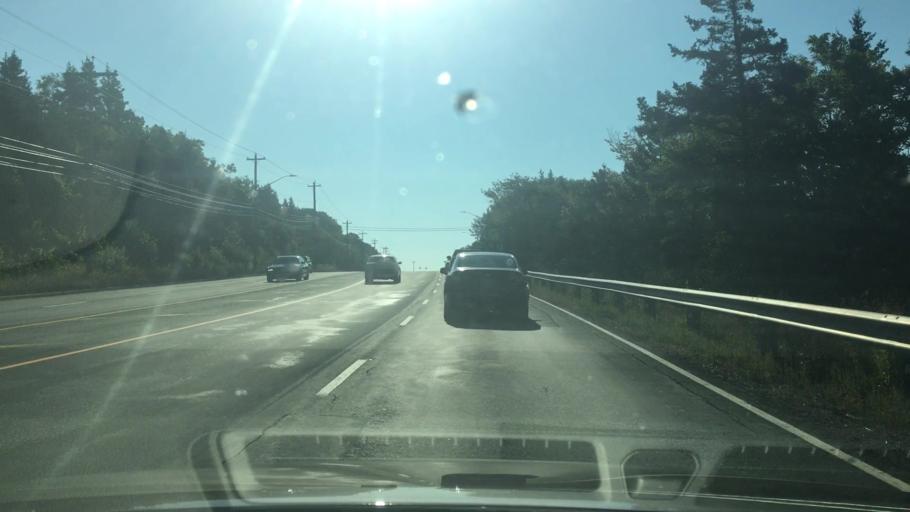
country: CA
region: Nova Scotia
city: Dartmouth
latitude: 44.7056
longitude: -63.6176
